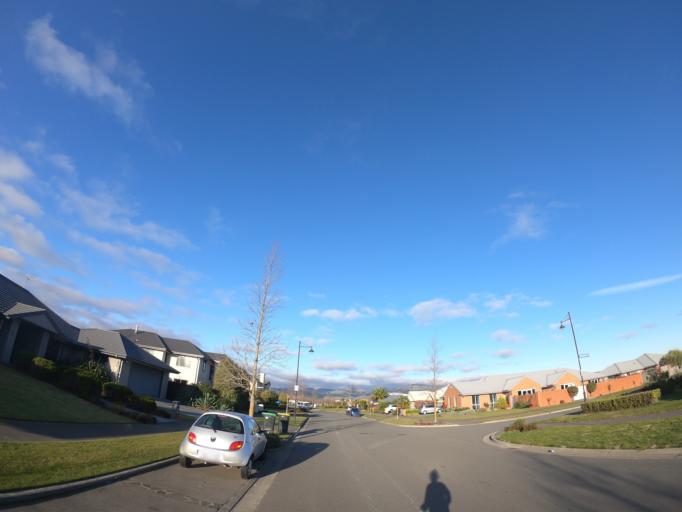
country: NZ
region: Canterbury
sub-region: Selwyn District
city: Prebbleton
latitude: -43.5665
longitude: 172.5650
